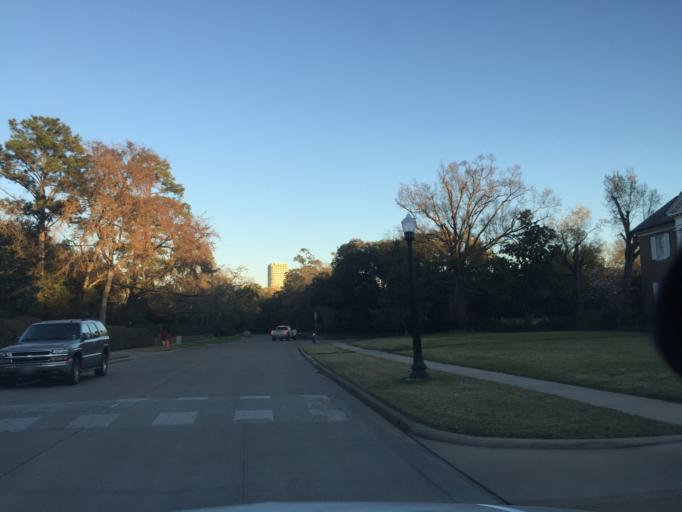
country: US
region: Texas
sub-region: Harris County
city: West University Place
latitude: 29.7516
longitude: -95.4311
